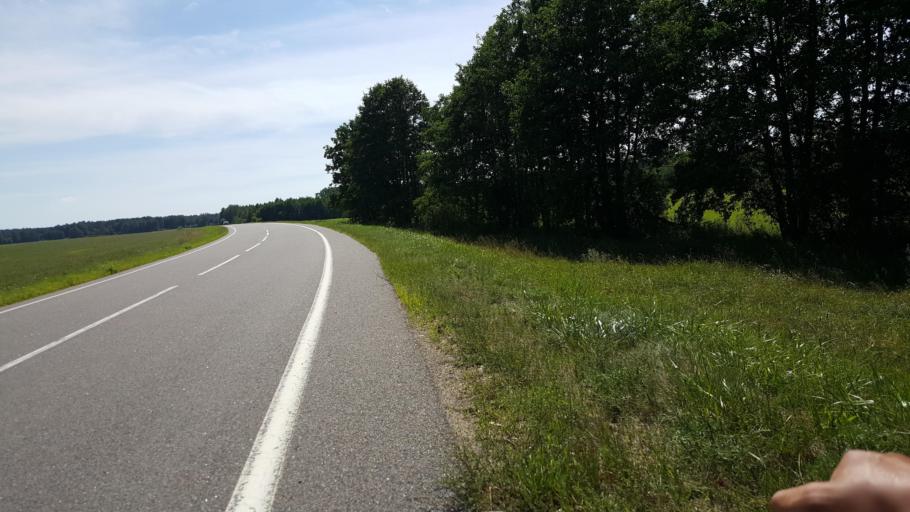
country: BY
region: Brest
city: Zhabinka
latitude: 52.4646
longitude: 24.1452
